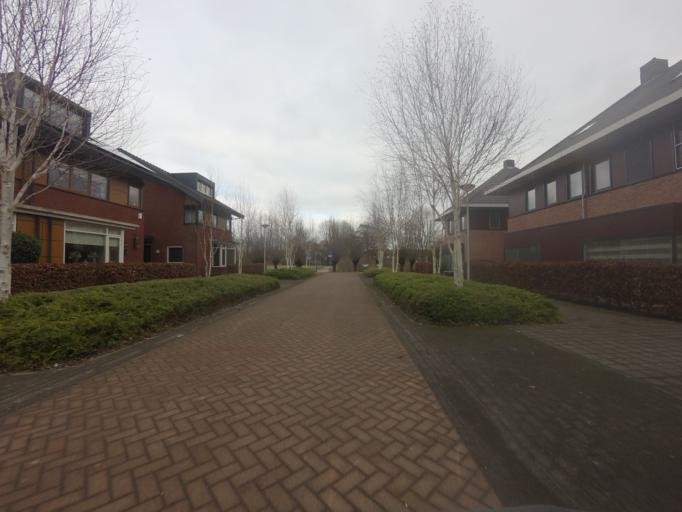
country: NL
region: Utrecht
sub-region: Stichtse Vecht
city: Spechtenkamp
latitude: 52.0784
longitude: 5.0239
